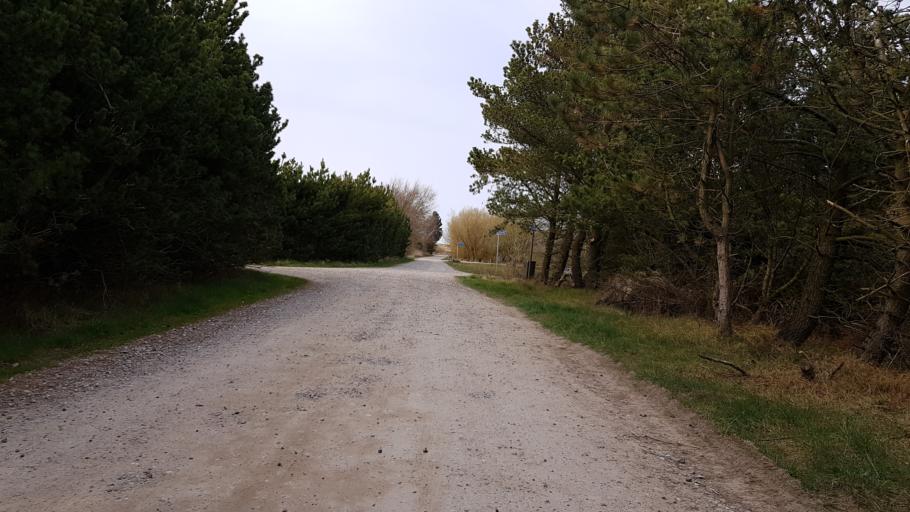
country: DE
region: Schleswig-Holstein
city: List
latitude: 55.1653
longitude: 8.5409
